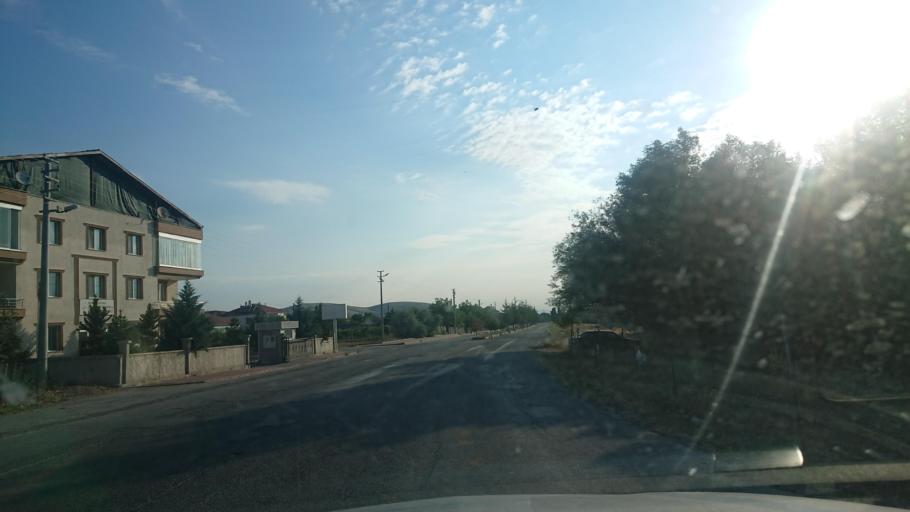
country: TR
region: Aksaray
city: Ortakoy
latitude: 38.7456
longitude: 34.0485
